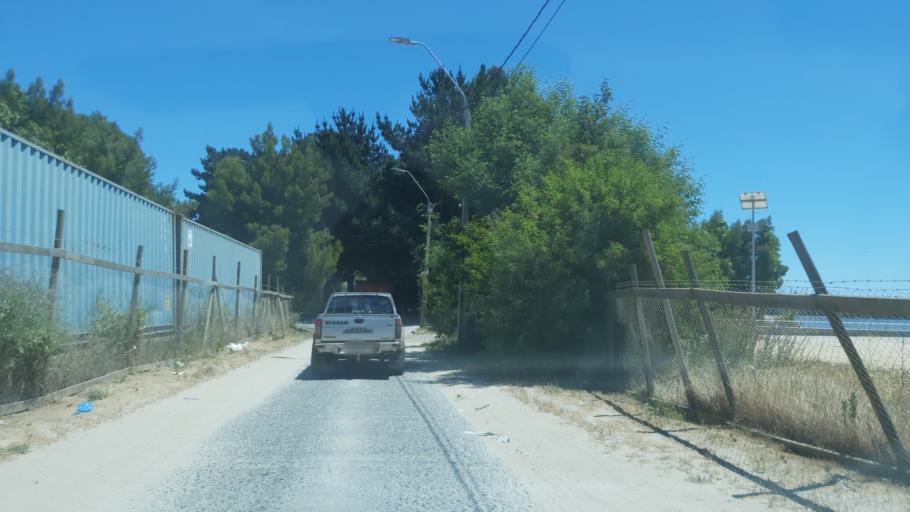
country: CL
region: Maule
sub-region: Provincia de Talca
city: Constitucion
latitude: -35.3390
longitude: -72.3988
